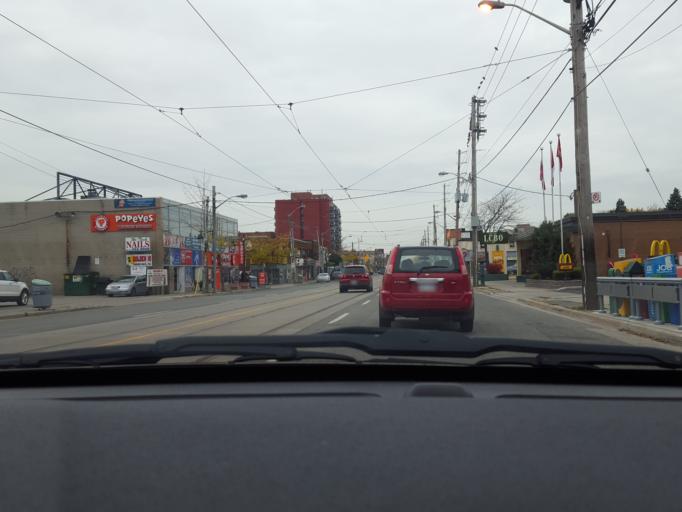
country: CA
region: Ontario
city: Etobicoke
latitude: 43.6023
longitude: -79.4985
